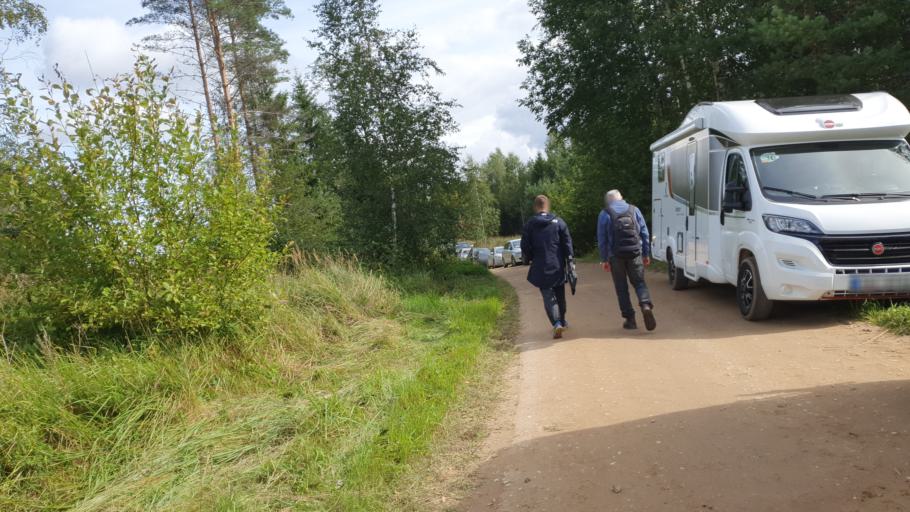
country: EE
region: Tartu
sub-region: UElenurme vald
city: Ulenurme
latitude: 58.1318
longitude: 26.7553
